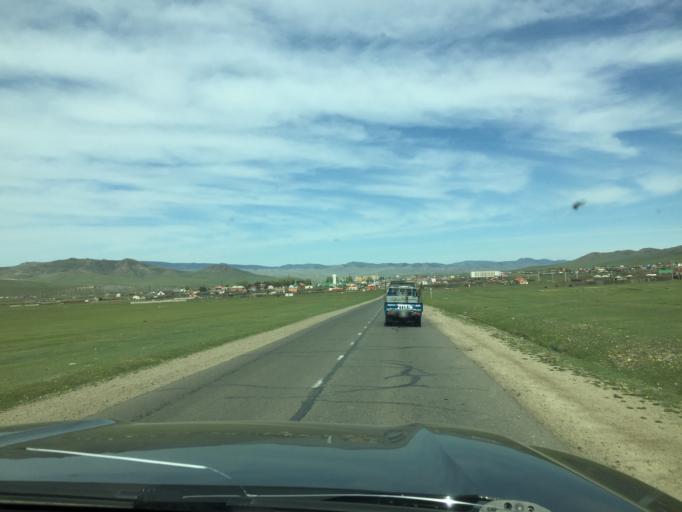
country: MN
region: Central Aimak
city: Ihsueuej
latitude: 48.2173
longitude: 106.3056
